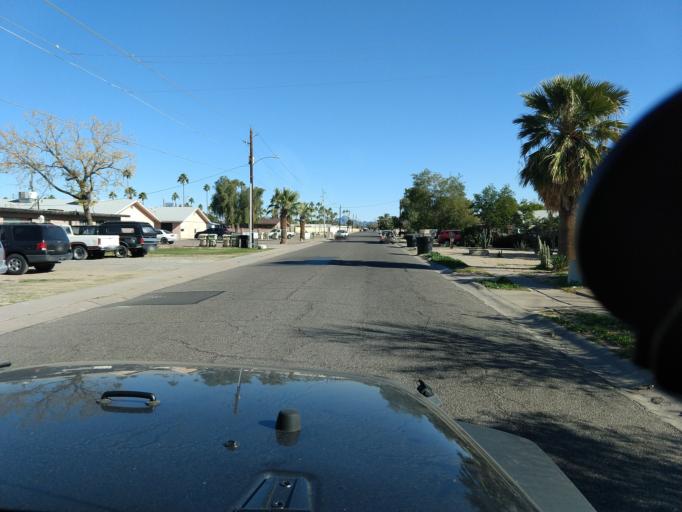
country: US
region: Arizona
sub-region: Maricopa County
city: Glendale
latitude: 33.5422
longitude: -112.1742
